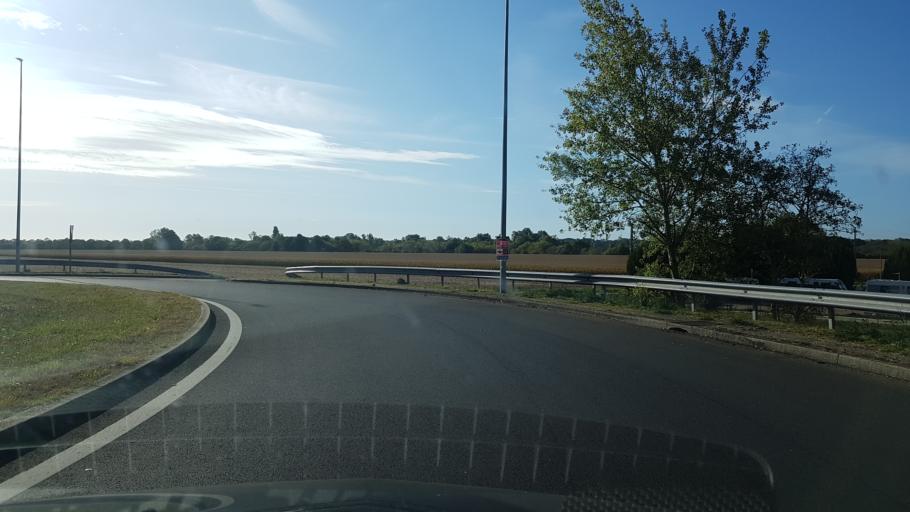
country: FR
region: Centre
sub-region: Departement du Loiret
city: Saint-Martin-sur-Ocre
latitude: 47.6703
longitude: 2.6768
